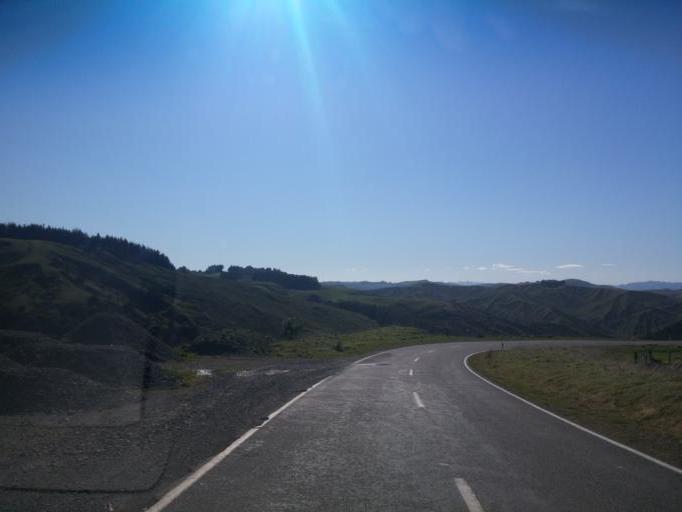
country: NZ
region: Wellington
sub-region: South Wairarapa District
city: Waipawa
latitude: -41.3610
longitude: 175.4982
